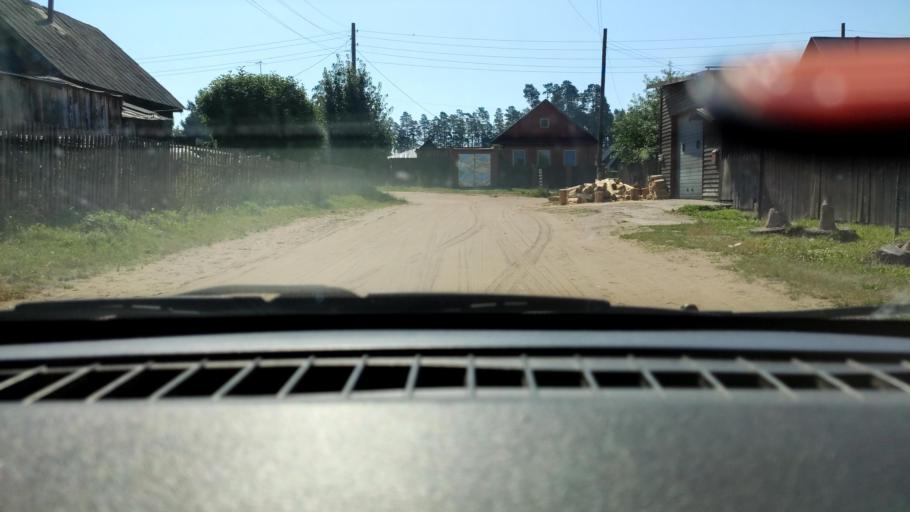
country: RU
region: Perm
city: Ust'-Kachka
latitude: 57.9325
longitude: 55.5167
